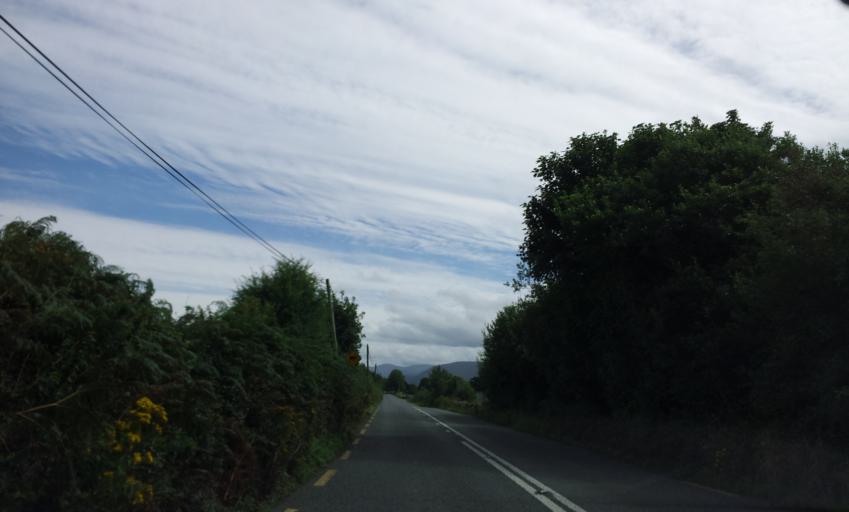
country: IE
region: Munster
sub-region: Ciarrai
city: Killorglin
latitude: 52.0909
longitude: -9.6904
